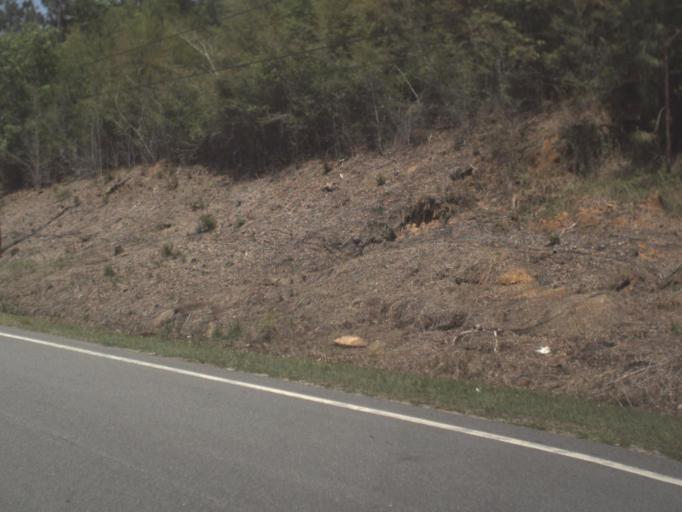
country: US
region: Florida
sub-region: Escambia County
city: Gonzalez
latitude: 30.5348
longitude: -87.3384
